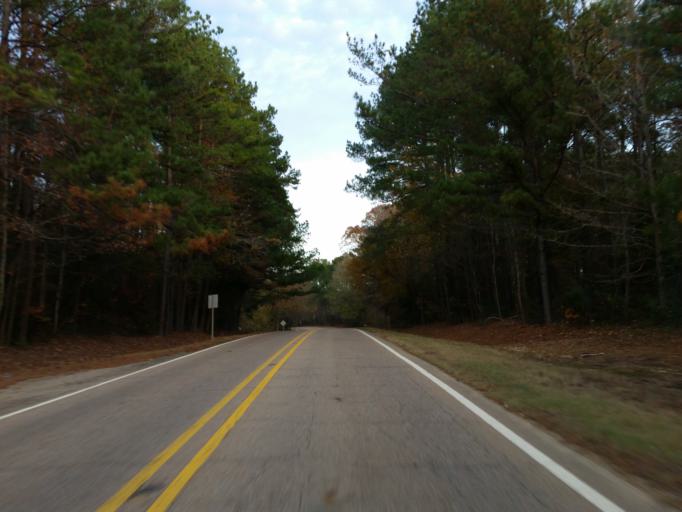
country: US
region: Alabama
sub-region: Sumter County
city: York
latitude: 32.4244
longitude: -88.4120
